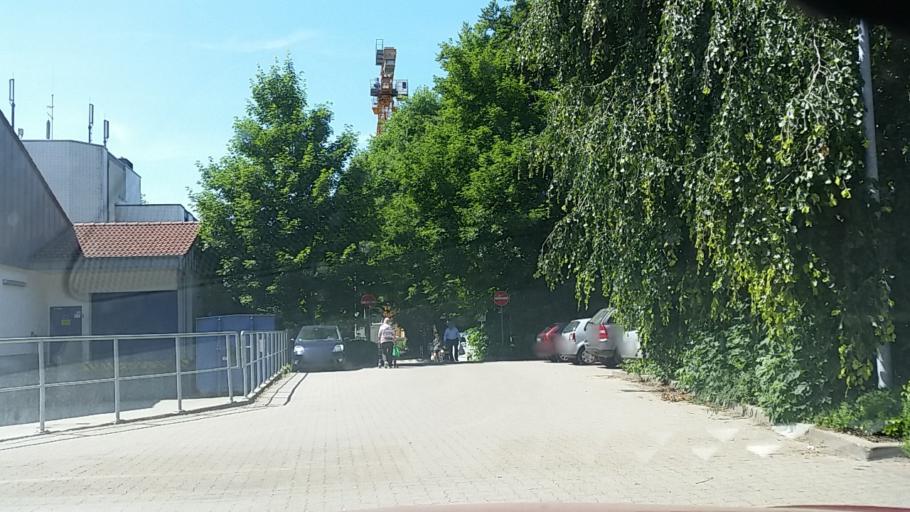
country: DE
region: Schleswig-Holstein
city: Rellingen
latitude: 53.5809
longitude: 9.7980
